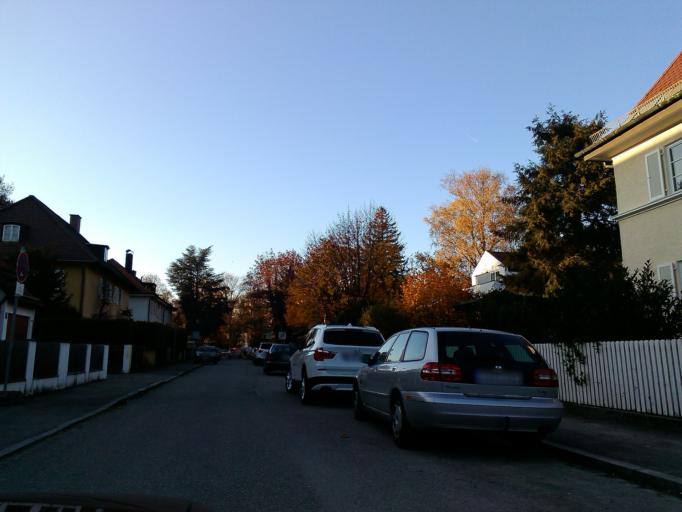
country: DE
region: Bavaria
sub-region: Upper Bavaria
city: Pasing
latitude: 48.1408
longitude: 11.4501
